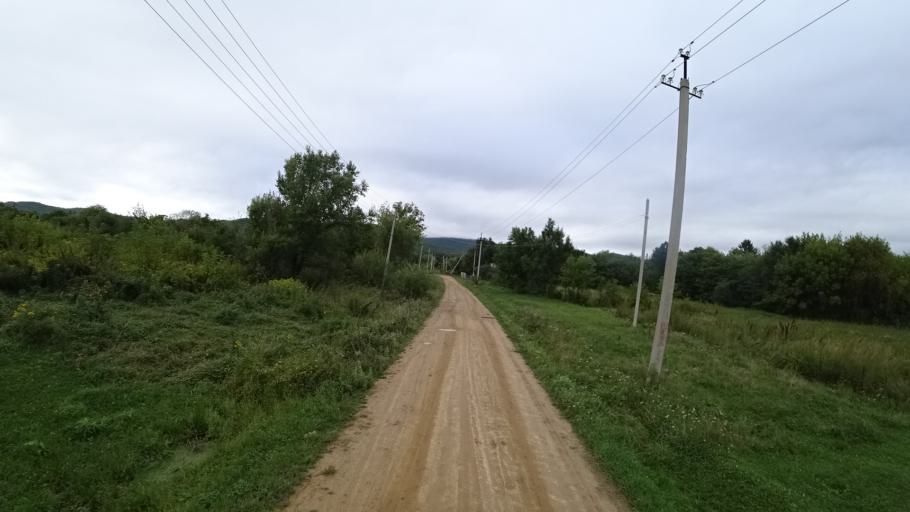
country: RU
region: Primorskiy
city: Rettikhovka
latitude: 44.1405
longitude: 132.6416
